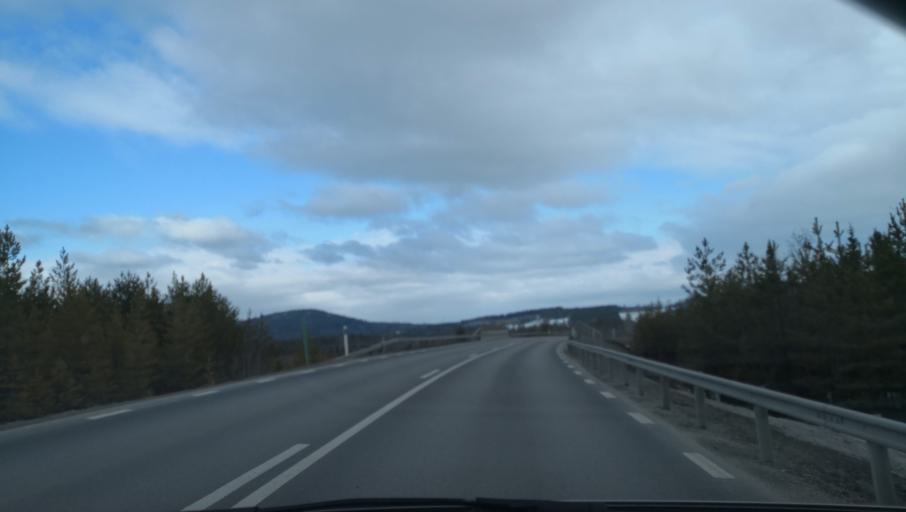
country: SE
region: Vaesterbotten
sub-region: Vannas Kommun
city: Vaennaes
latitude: 63.9224
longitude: 19.7435
